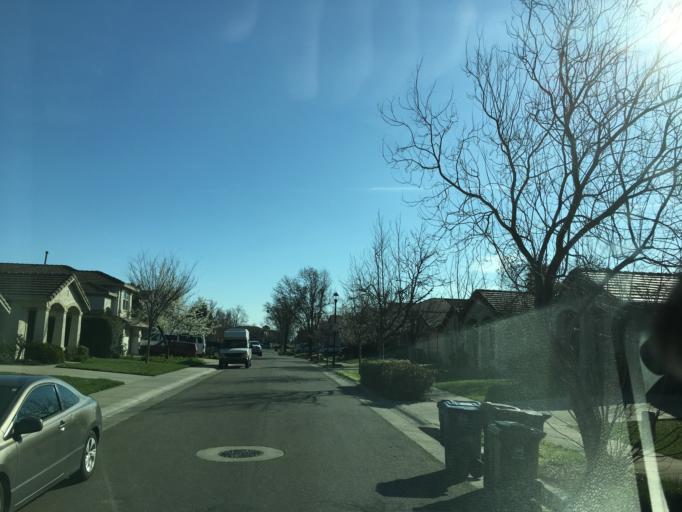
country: US
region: California
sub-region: Yolo County
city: Davis
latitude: 38.5575
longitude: -121.7012
